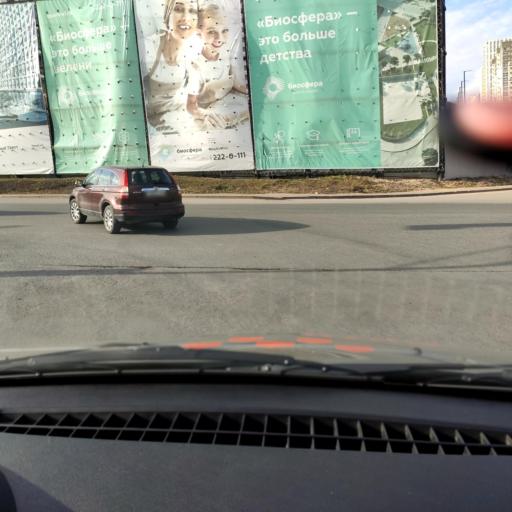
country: RU
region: Bashkortostan
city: Ufa
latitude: 54.7605
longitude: 56.0363
